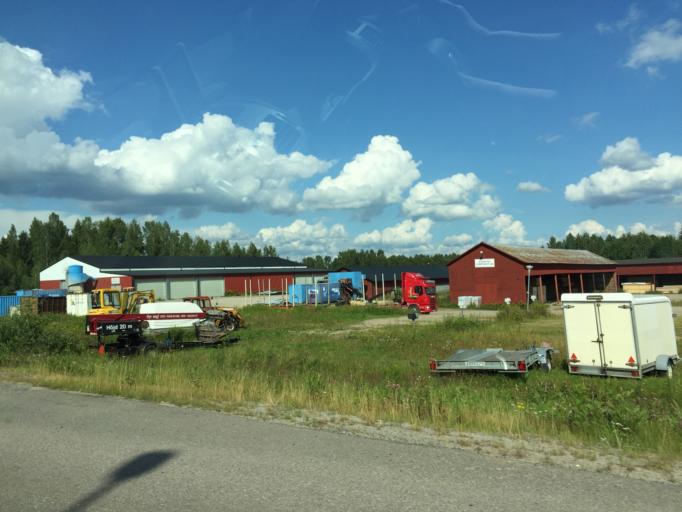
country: SE
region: Gaevleborg
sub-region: Bollnas Kommun
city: Arbra
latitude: 61.4632
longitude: 16.3688
